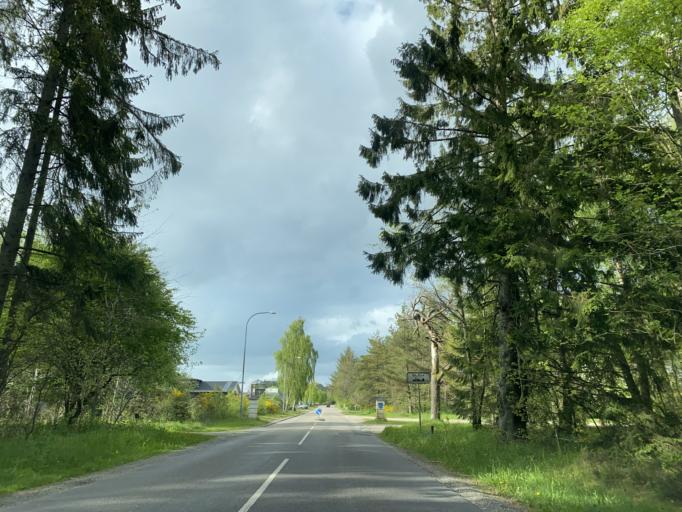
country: DK
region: Central Jutland
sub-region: Skanderborg Kommune
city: Ry
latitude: 56.0645
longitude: 9.6931
